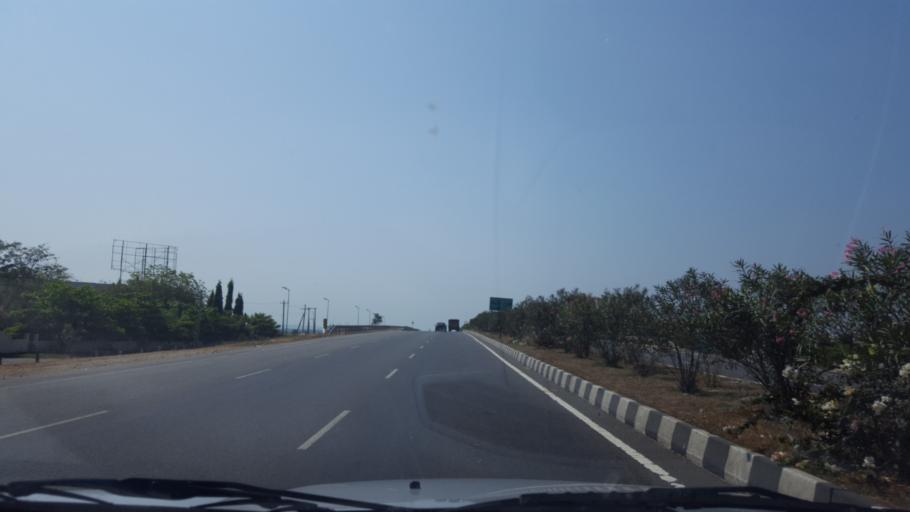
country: IN
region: Andhra Pradesh
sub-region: Guntur
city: Chilakalurupet
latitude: 16.0469
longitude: 80.1402
